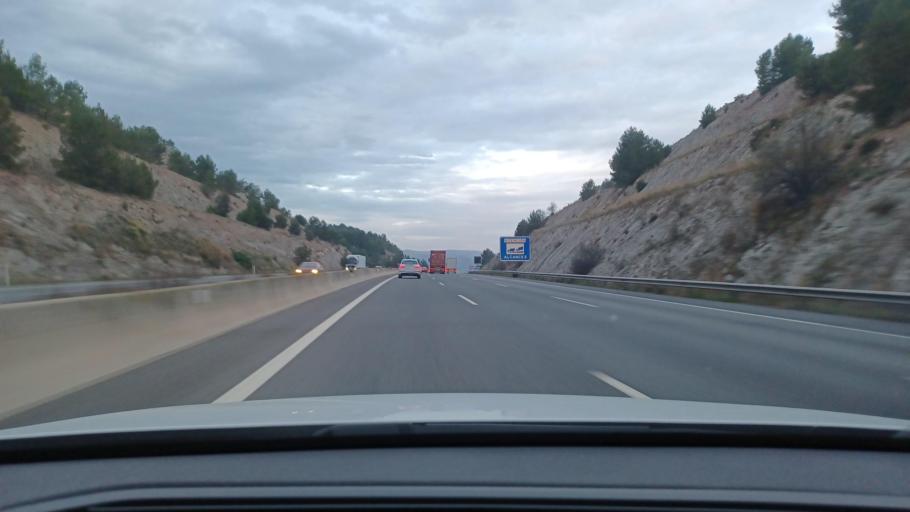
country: ES
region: Valencia
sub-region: Provincia de Valencia
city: Llosa de Ranes
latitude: 39.0329
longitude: -0.5514
